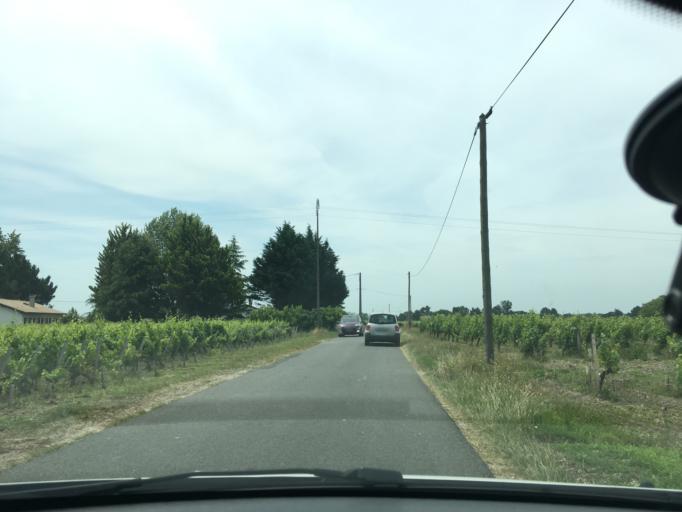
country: FR
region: Aquitaine
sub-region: Departement de la Gironde
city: Listrac-Medoc
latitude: 45.0683
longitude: -0.7961
